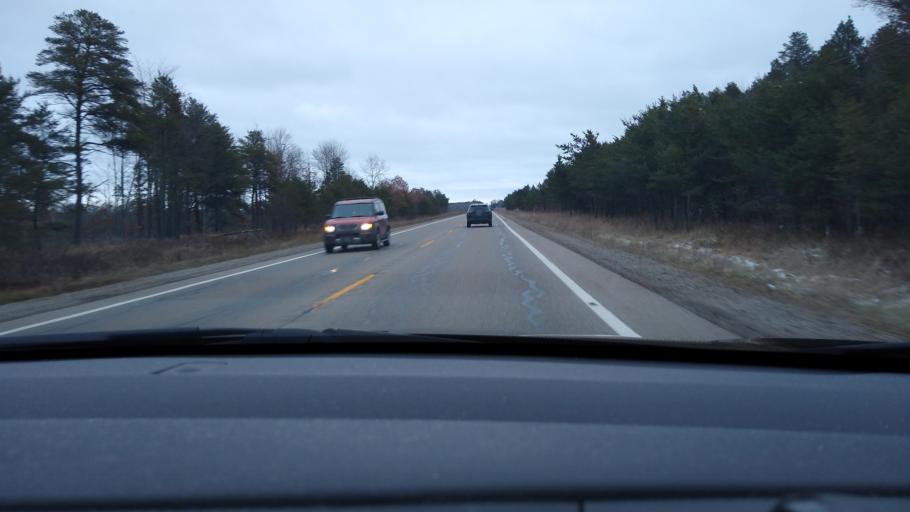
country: US
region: Michigan
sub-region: Roscommon County
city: Houghton Lake
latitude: 44.3358
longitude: -84.8410
